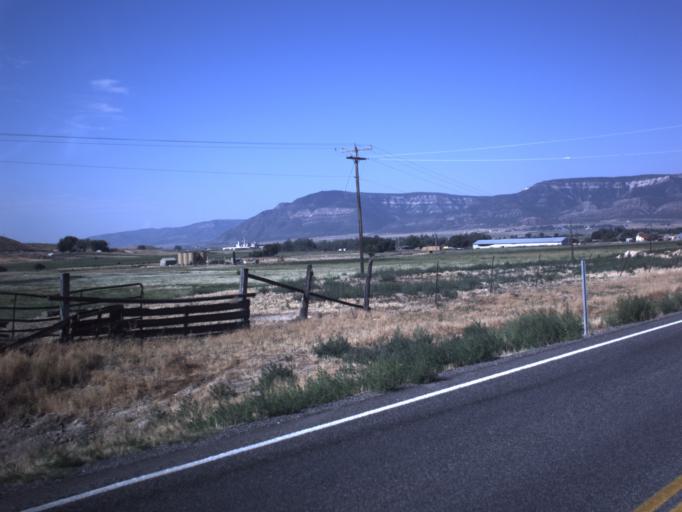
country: US
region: Utah
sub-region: Sanpete County
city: Moroni
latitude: 39.5253
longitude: -111.5583
